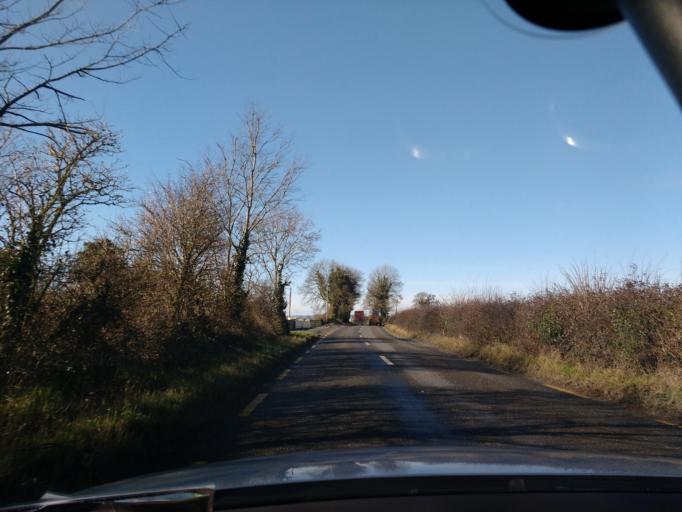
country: IE
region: Munster
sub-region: North Tipperary
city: Nenagh
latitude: 52.8318
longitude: -8.1034
